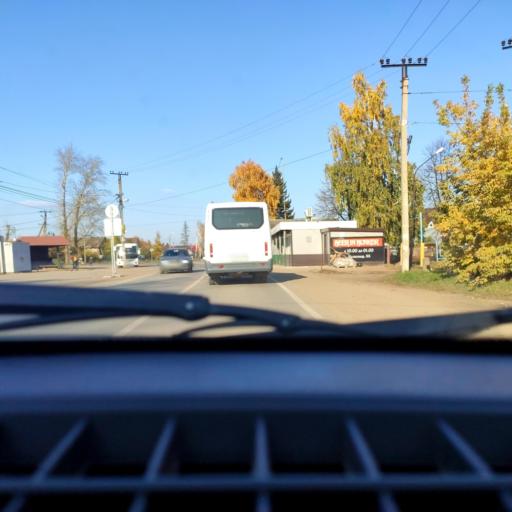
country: RU
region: Bashkortostan
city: Iglino
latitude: 54.8263
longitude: 56.1849
